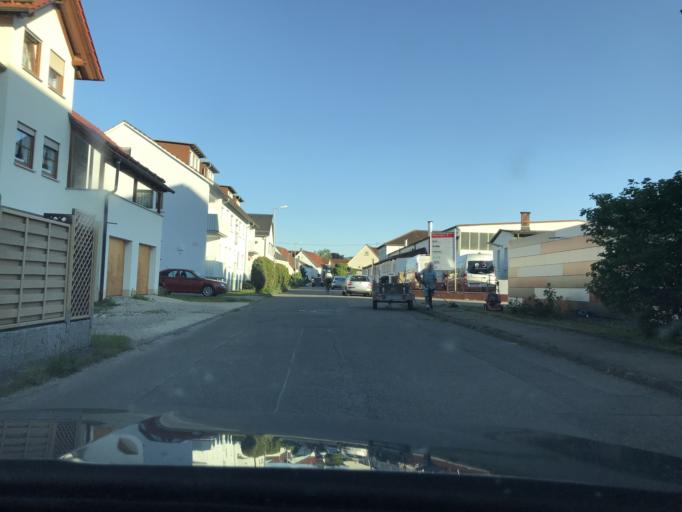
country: DE
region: Baden-Wuerttemberg
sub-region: Regierungsbezirk Stuttgart
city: Owen
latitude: 48.5900
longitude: 9.4463
